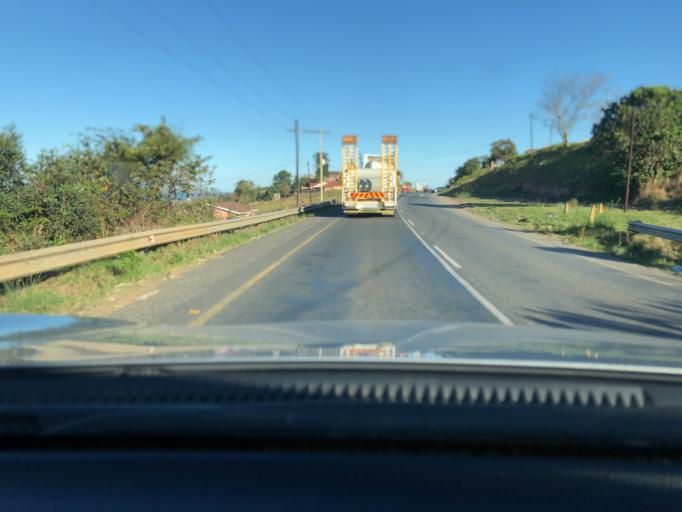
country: ZA
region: KwaZulu-Natal
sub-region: eThekwini Metropolitan Municipality
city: Umkomaas
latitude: -30.0152
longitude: 30.8076
